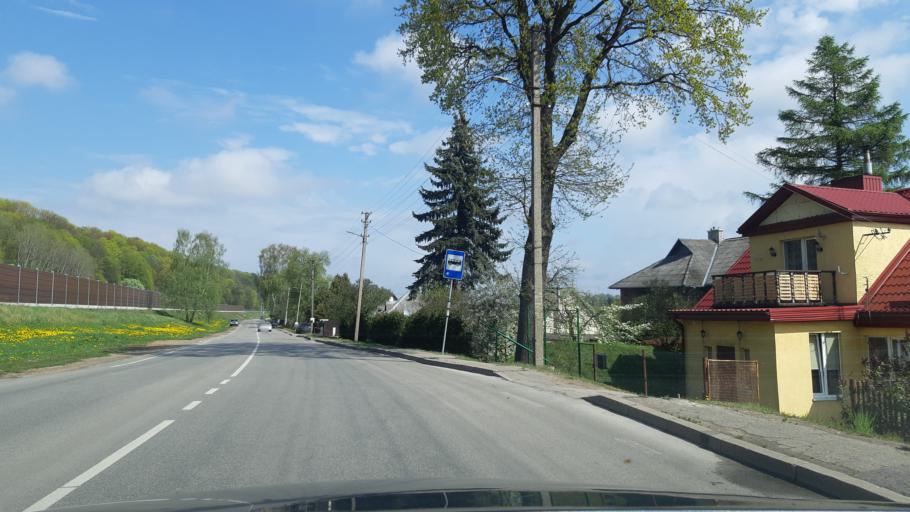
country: LT
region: Kauno apskritis
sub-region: Kaunas
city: Aleksotas
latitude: 54.8636
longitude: 23.9257
